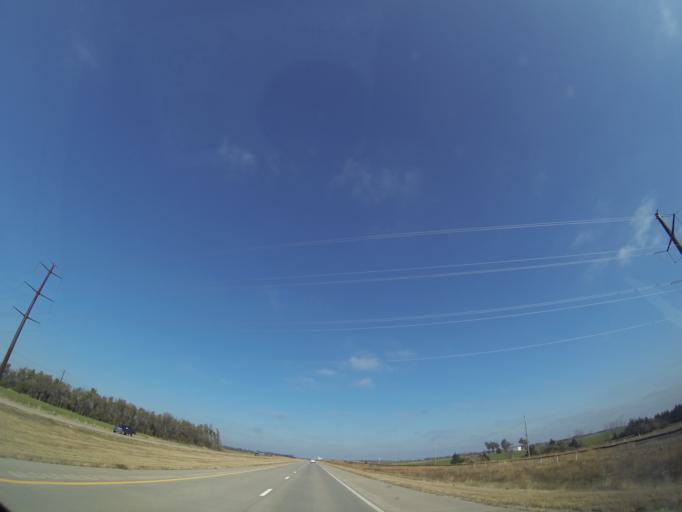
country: US
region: Kansas
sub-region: McPherson County
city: Inman
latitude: 38.2008
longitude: -97.8018
